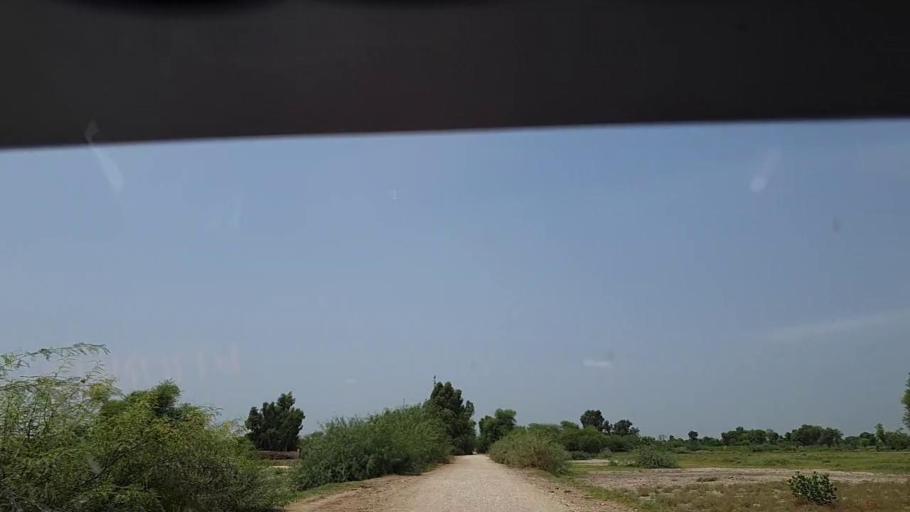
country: PK
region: Sindh
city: Pano Aqil
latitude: 27.9161
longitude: 69.2072
